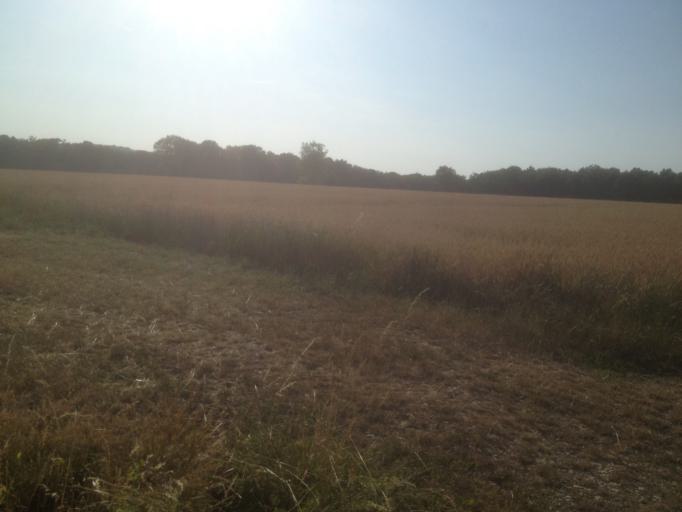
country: FR
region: Champagne-Ardenne
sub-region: Departement de la Haute-Marne
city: Doulaincourt-Saucourt
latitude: 48.4532
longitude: 5.3303
